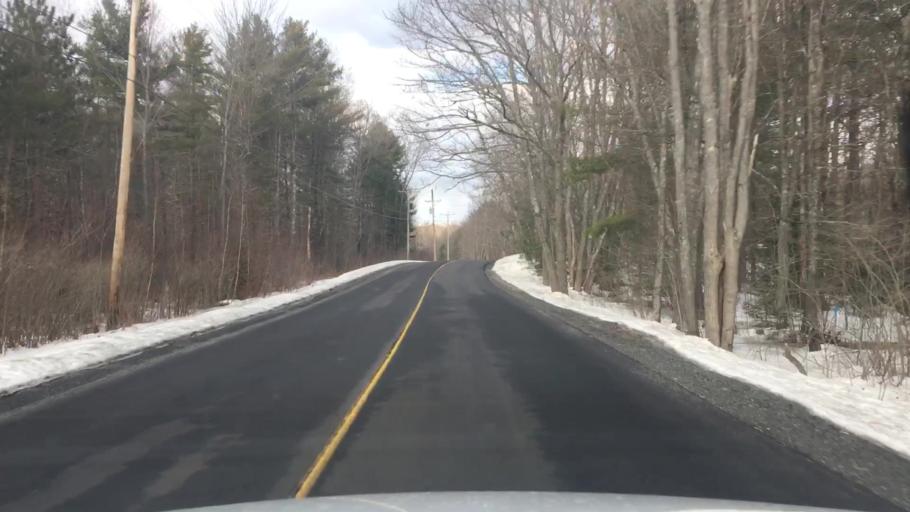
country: US
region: Maine
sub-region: York County
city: Arundel
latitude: 43.4203
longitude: -70.4621
